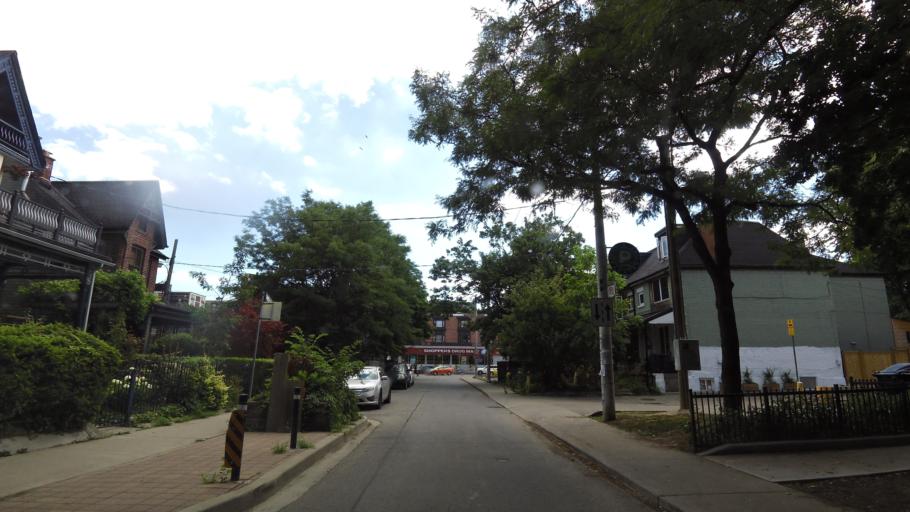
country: CA
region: Ontario
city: Toronto
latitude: 43.6408
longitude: -79.4393
